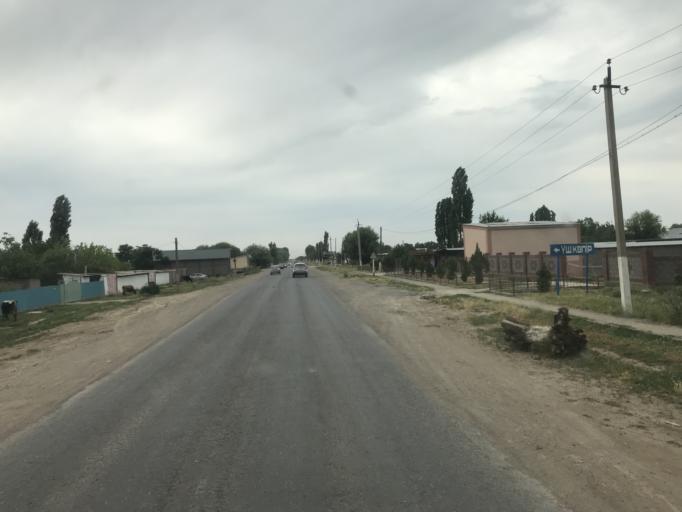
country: KZ
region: Ongtustik Qazaqstan
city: Asykata
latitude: 40.9026
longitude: 68.3572
